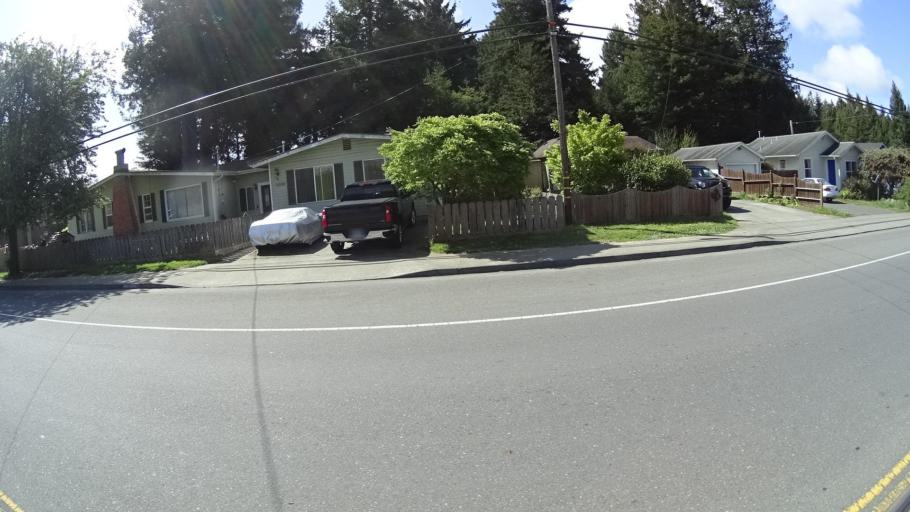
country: US
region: California
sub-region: Humboldt County
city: Cutten
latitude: 40.7733
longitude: -124.1441
